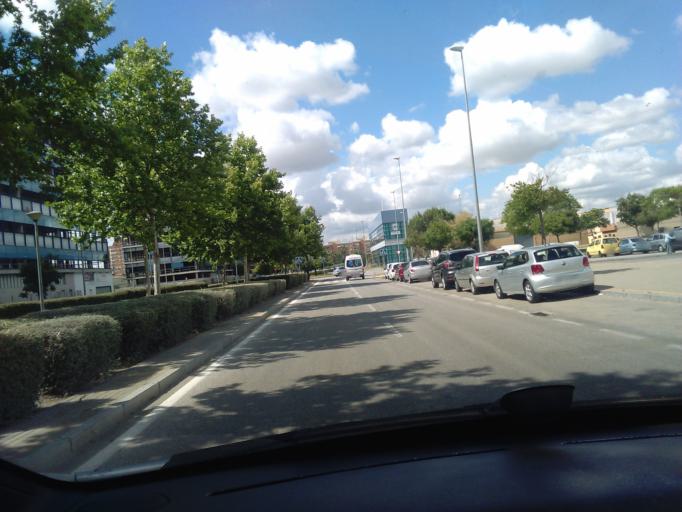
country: ES
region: Andalusia
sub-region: Provincia de Sevilla
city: Sevilla
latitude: 37.3831
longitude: -5.9191
